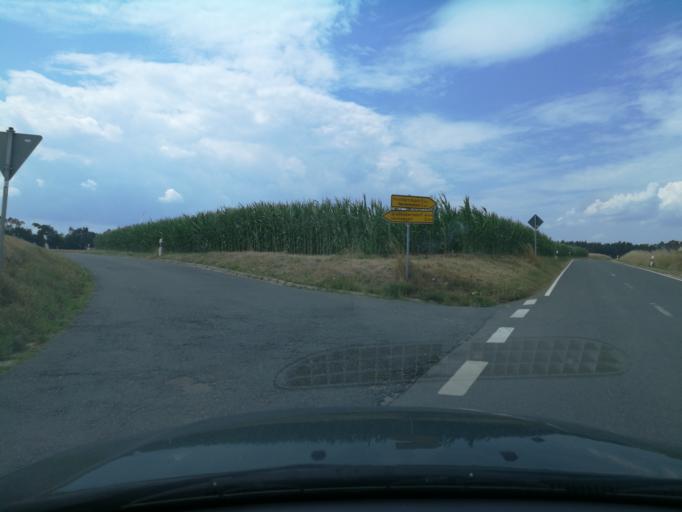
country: DE
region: Bavaria
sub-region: Regierungsbezirk Mittelfranken
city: Grosshabersdorf
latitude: 49.4380
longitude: 10.7910
